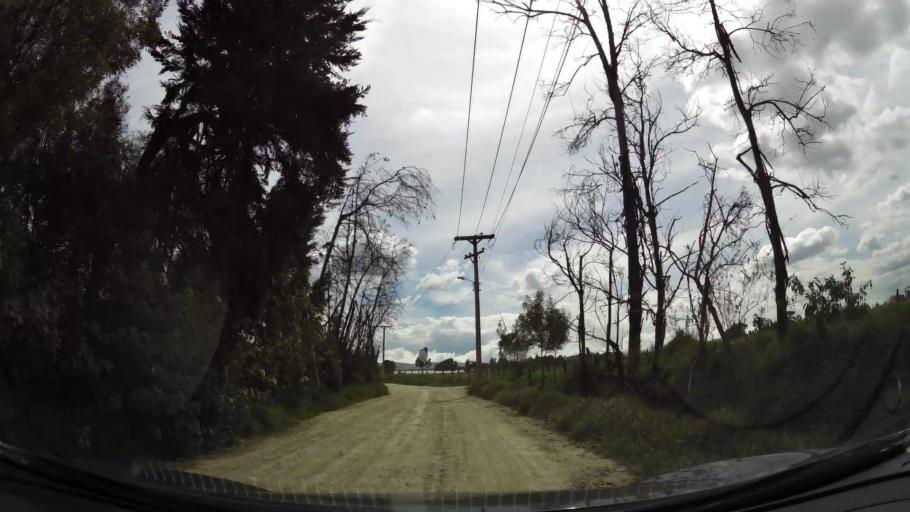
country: CO
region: Cundinamarca
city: Funza
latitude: 4.7072
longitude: -74.1781
